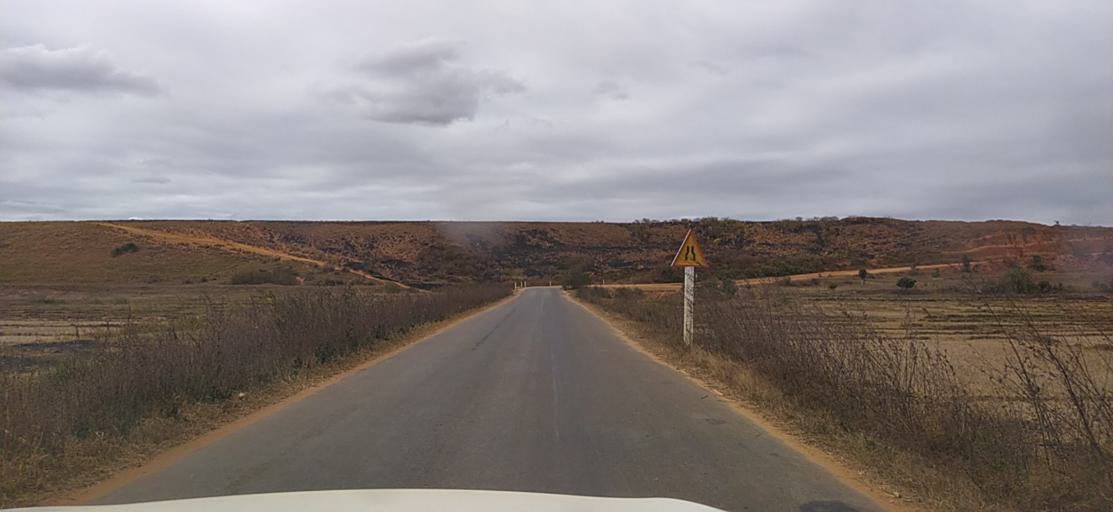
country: MG
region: Alaotra Mangoro
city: Ambatondrazaka
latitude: -17.9131
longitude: 48.2606
